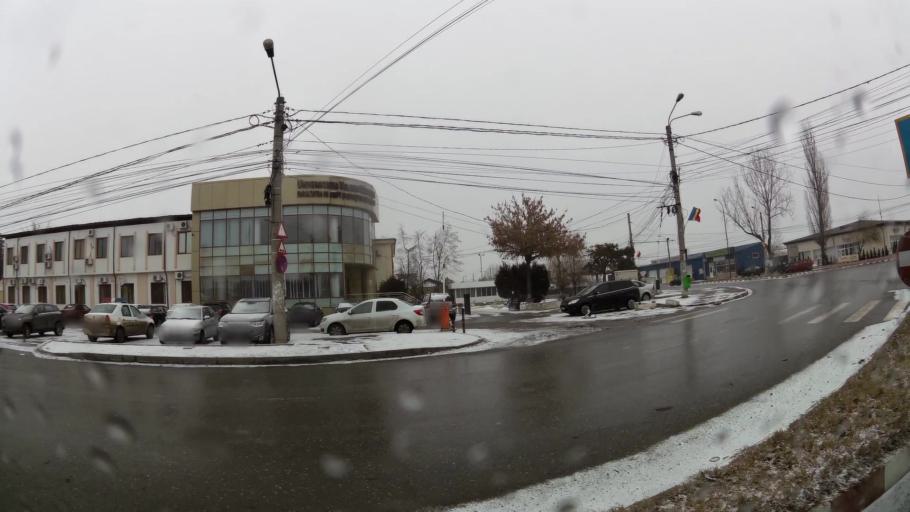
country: RO
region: Dambovita
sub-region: Municipiul Targoviste
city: Targoviste
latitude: 44.9115
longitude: 25.4497
